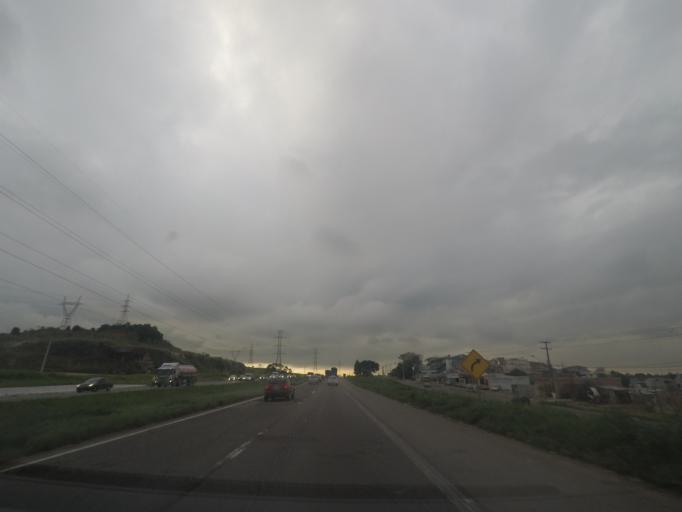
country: BR
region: Parana
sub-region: Curitiba
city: Curitiba
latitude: -25.5104
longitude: -49.3390
